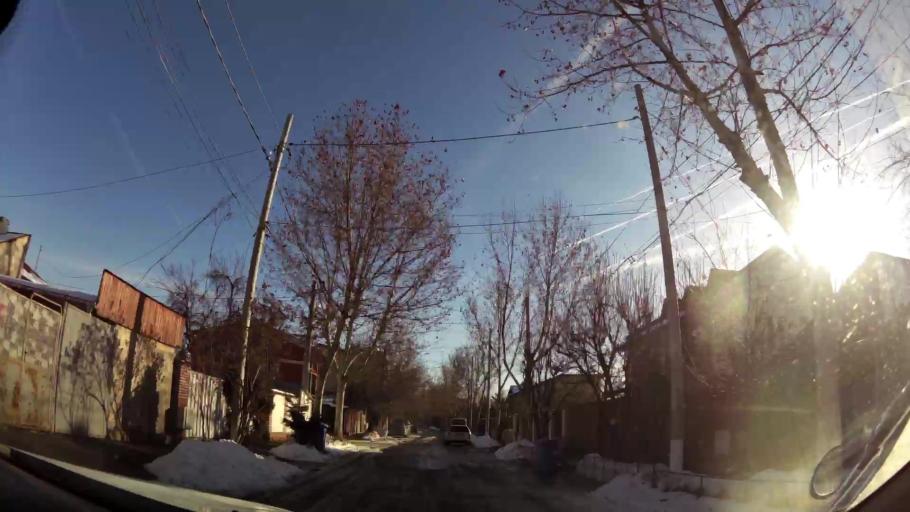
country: RO
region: Ilfov
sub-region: Comuna Fundeni-Dobroesti
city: Fundeni
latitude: 44.4786
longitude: 26.1524
